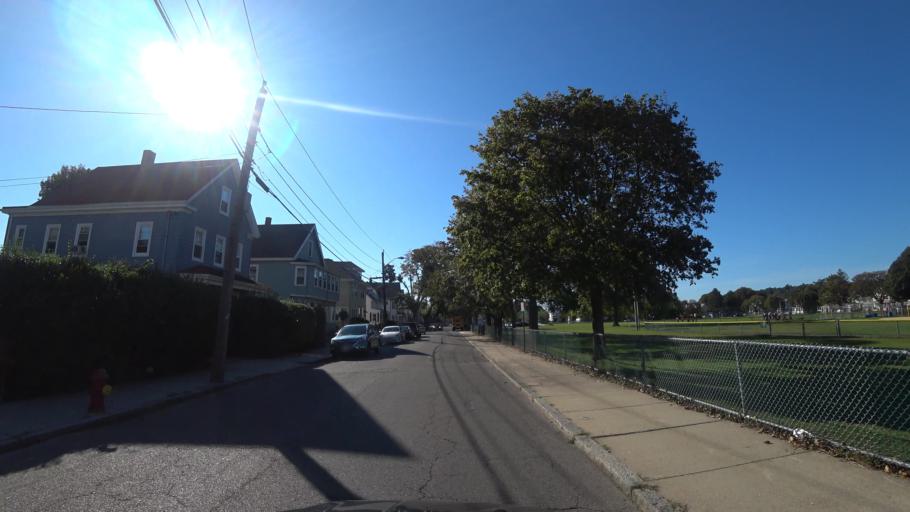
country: US
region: Massachusetts
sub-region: Middlesex County
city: Malden
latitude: 42.4196
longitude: -71.0830
